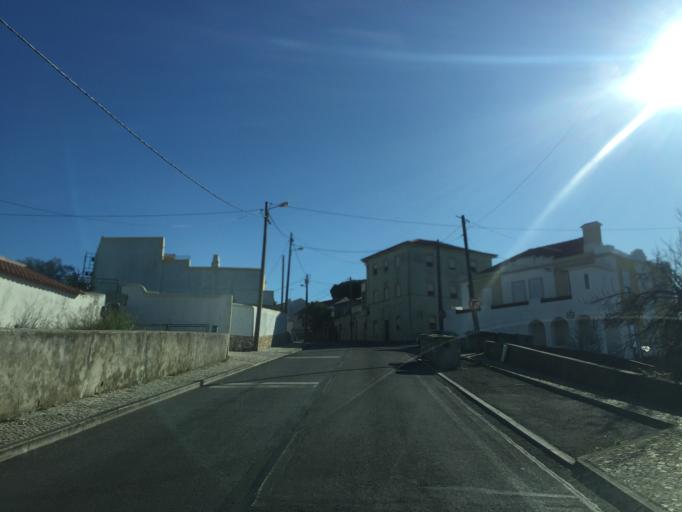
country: PT
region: Lisbon
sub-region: Sintra
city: Almargem
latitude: 38.8254
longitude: -9.2985
